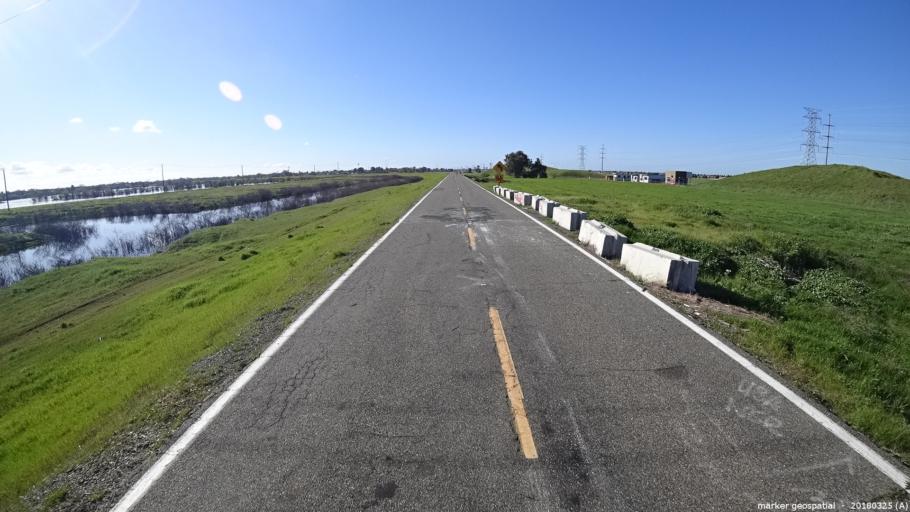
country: US
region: California
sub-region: Sacramento County
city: Rio Linda
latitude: 38.6780
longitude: -121.4855
